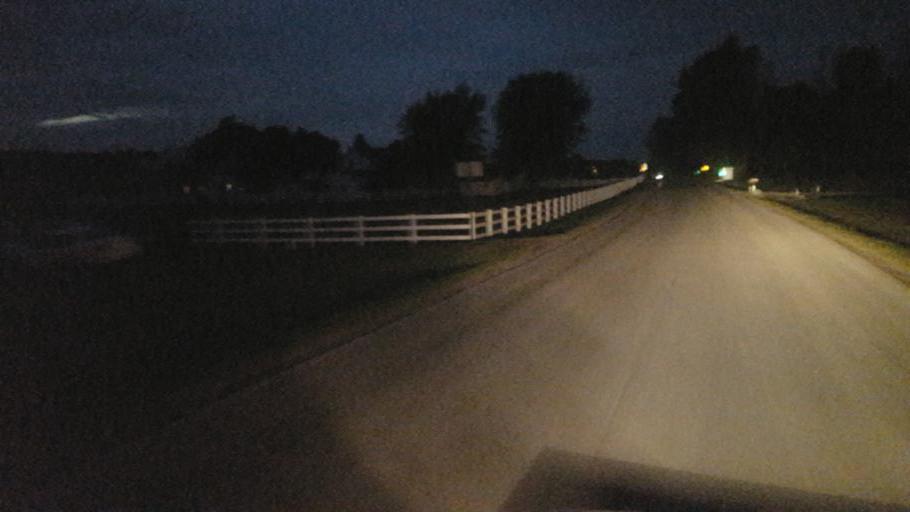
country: US
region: Ohio
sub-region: Wayne County
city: Apple Creek
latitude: 40.6989
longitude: -81.7929
